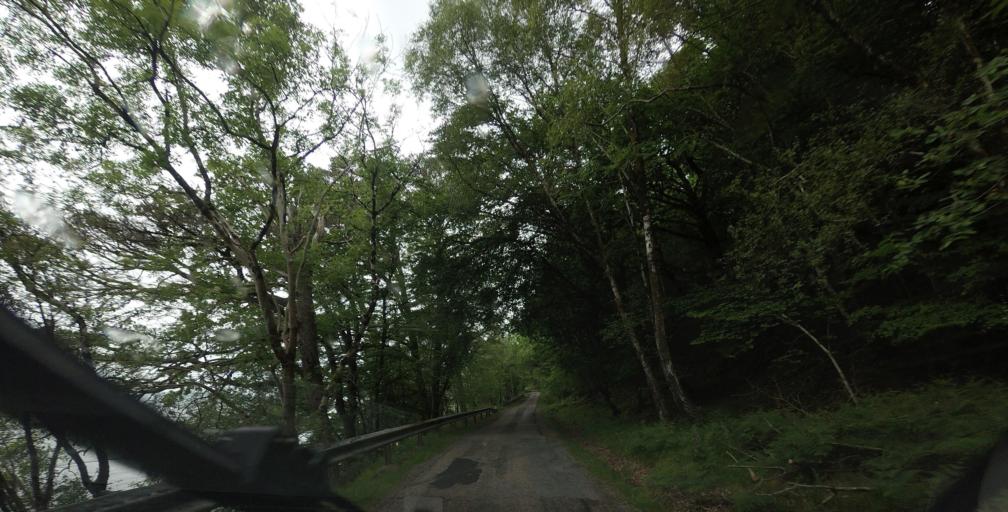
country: GB
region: Scotland
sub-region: Highland
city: Fort William
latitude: 56.7897
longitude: -5.1771
